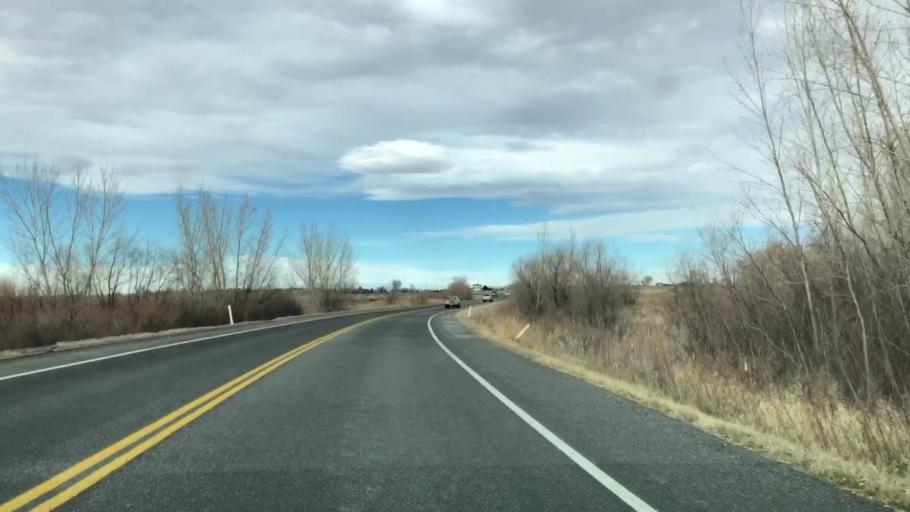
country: US
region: Colorado
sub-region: Weld County
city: Windsor
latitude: 40.5122
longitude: -104.9273
